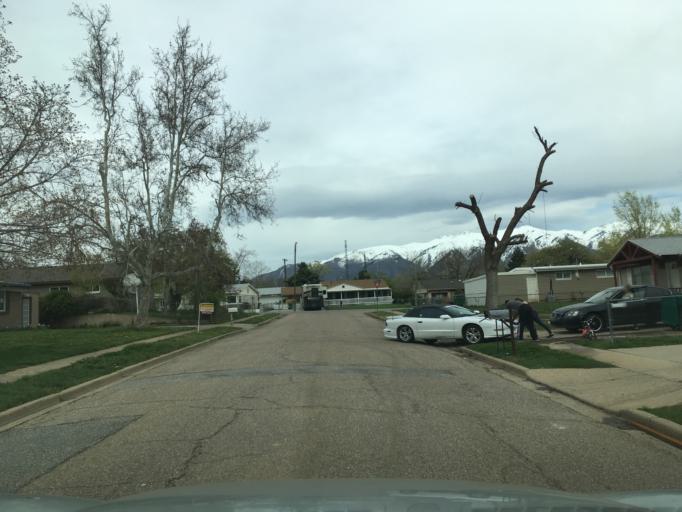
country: US
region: Utah
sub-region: Davis County
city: Layton
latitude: 41.0806
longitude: -111.9965
